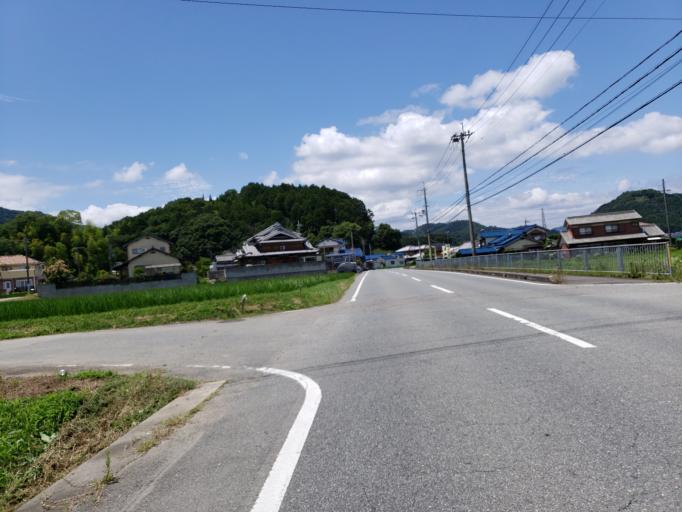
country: JP
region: Hyogo
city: Himeji
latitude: 34.9338
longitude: 134.7243
